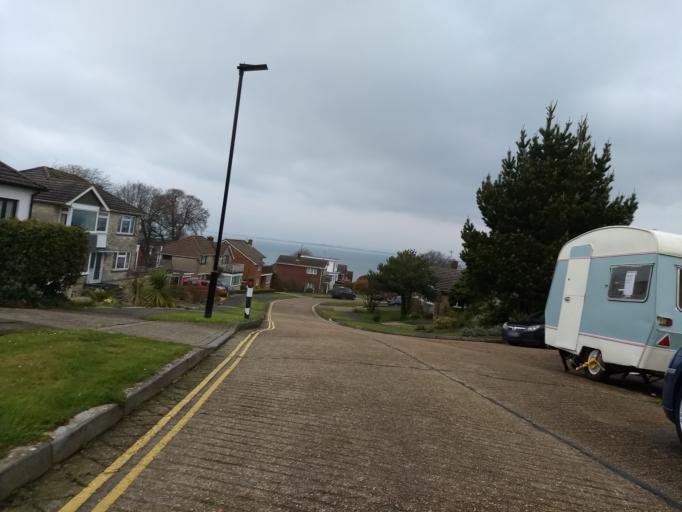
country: GB
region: England
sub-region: Isle of Wight
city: Ryde
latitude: 50.7313
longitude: -1.1684
